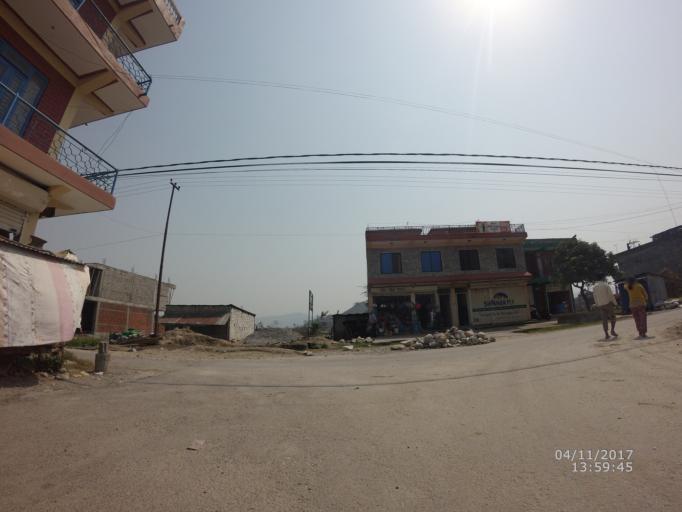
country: NP
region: Western Region
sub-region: Gandaki Zone
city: Pokhara
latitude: 28.1849
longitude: 84.0434
